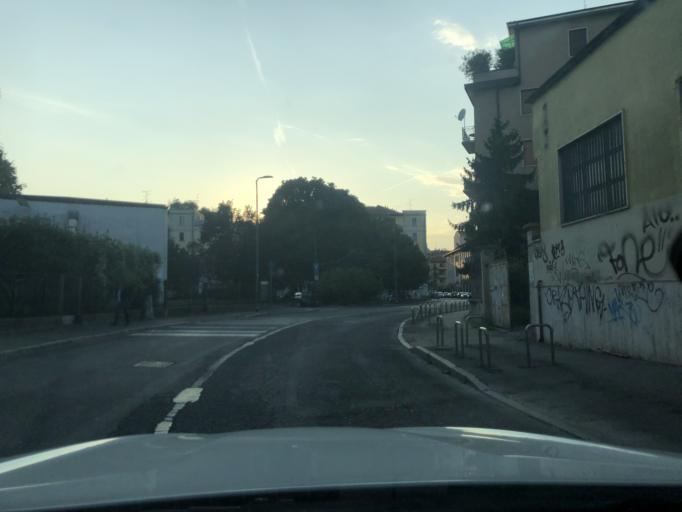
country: IT
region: Lombardy
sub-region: Citta metropolitana di Milano
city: Bresso
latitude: 45.5069
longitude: 9.2054
